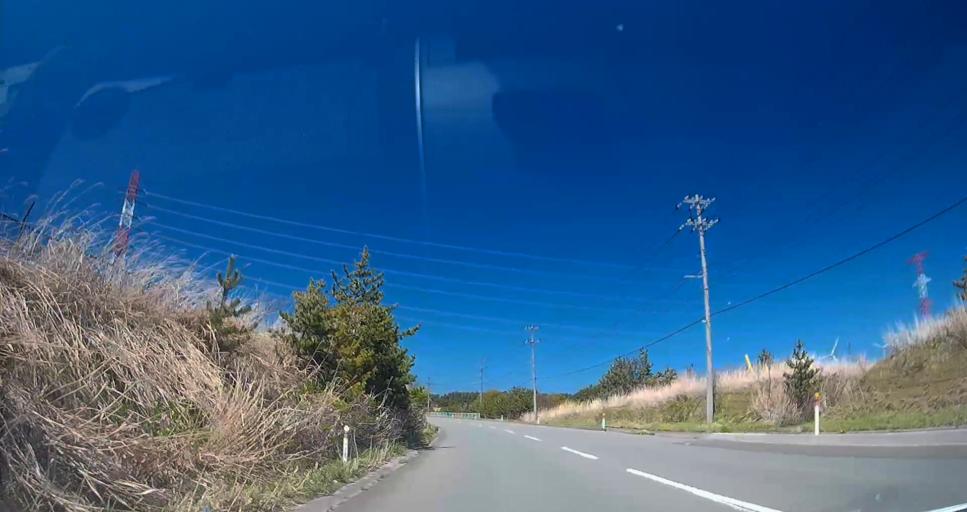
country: JP
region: Hokkaido
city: Hakodate
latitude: 41.5097
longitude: 140.9191
